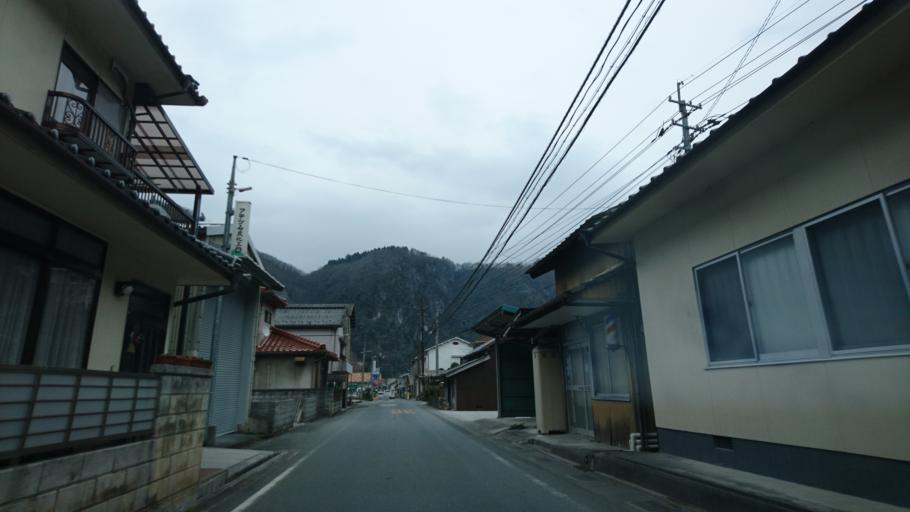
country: JP
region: Okayama
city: Niimi
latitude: 34.9314
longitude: 133.5152
